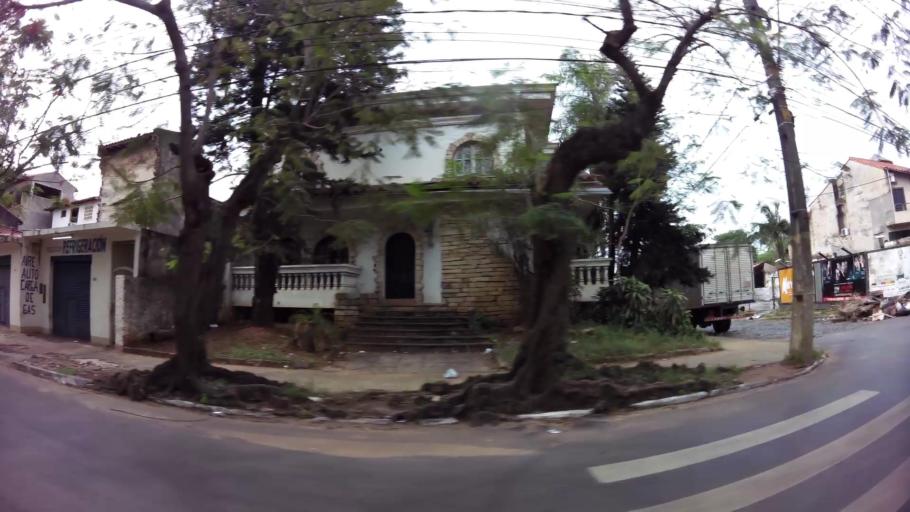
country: PY
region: Central
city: Fernando de la Mora
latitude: -25.2925
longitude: -57.5638
